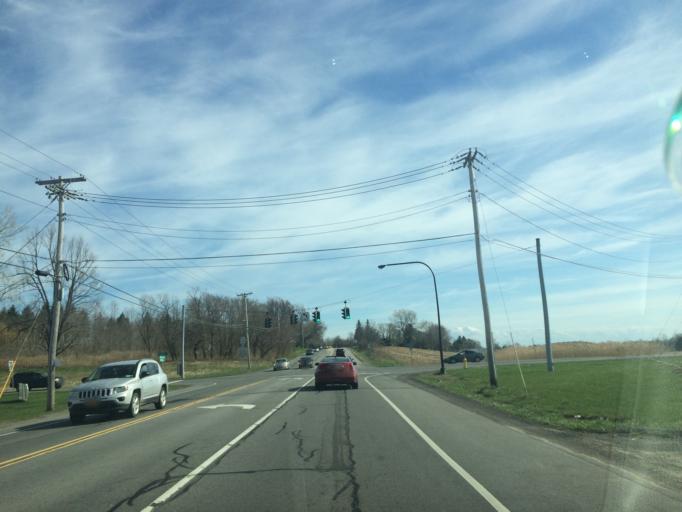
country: US
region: New York
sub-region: Monroe County
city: Webster
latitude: 43.1608
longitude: -77.4316
